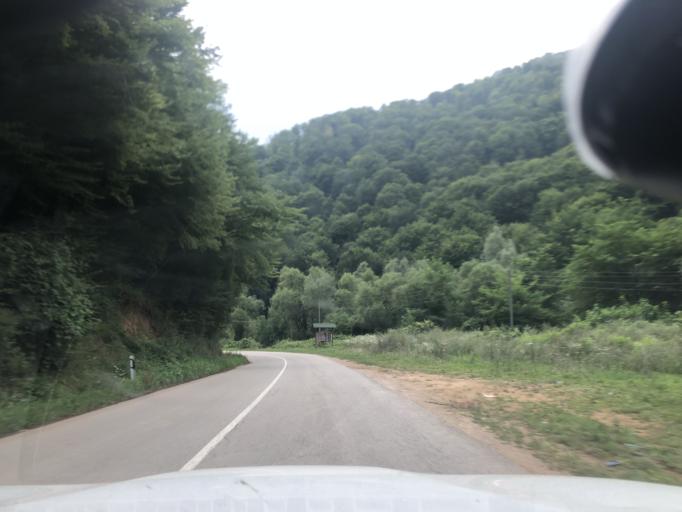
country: RS
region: Central Serbia
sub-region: Jablanicki Okrug
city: Medvega
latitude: 42.7806
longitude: 21.5974
